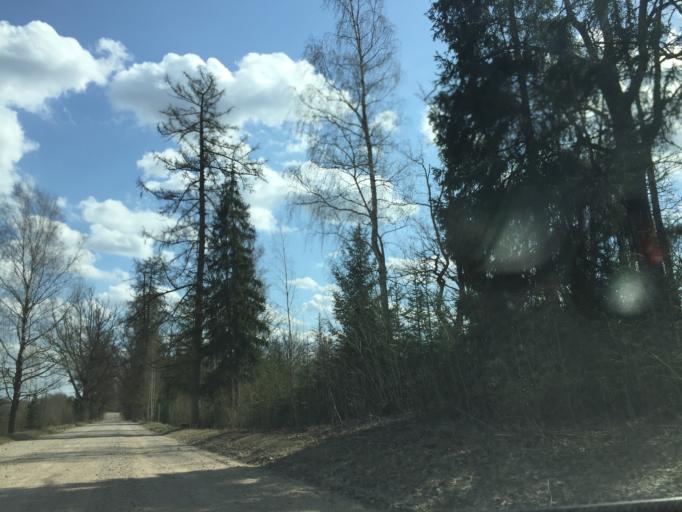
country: LV
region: Skriveri
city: Skriveri
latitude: 56.7528
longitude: 25.0798
